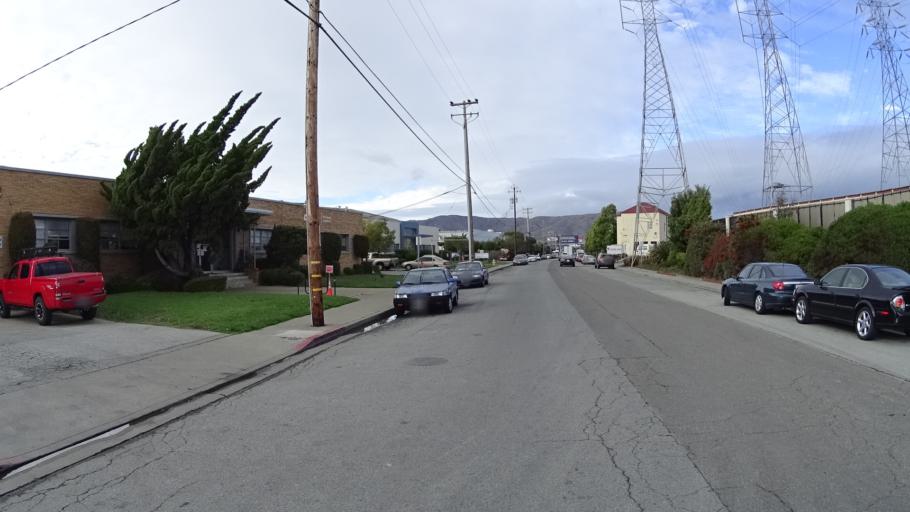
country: US
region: California
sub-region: San Mateo County
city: San Bruno
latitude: 37.6379
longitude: -122.4061
